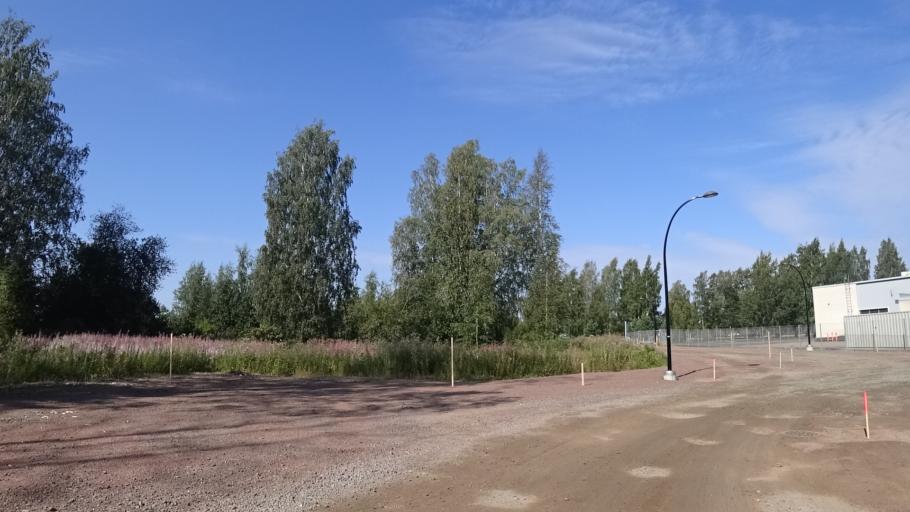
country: FI
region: Kymenlaakso
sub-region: Kotka-Hamina
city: Hamina
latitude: 60.5637
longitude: 27.1907
